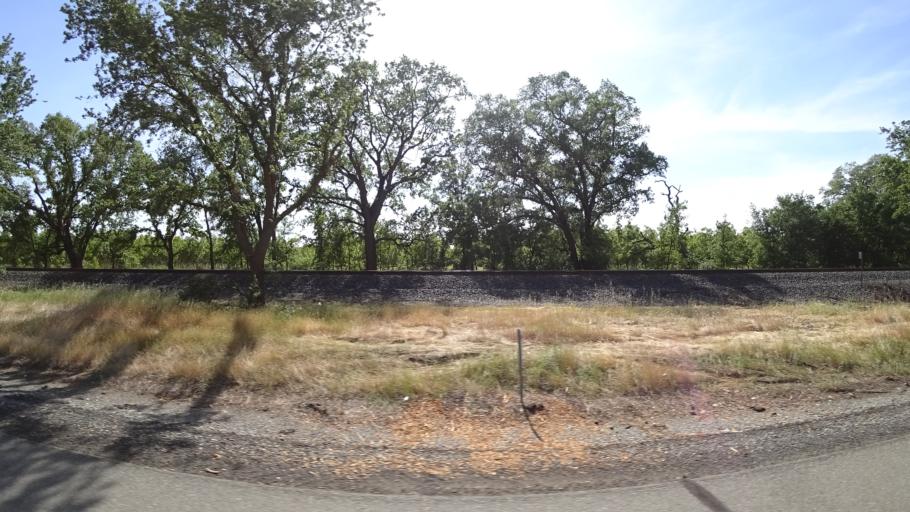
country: US
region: California
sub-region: Tehama County
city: Los Molinos
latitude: 39.9625
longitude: -122.0700
